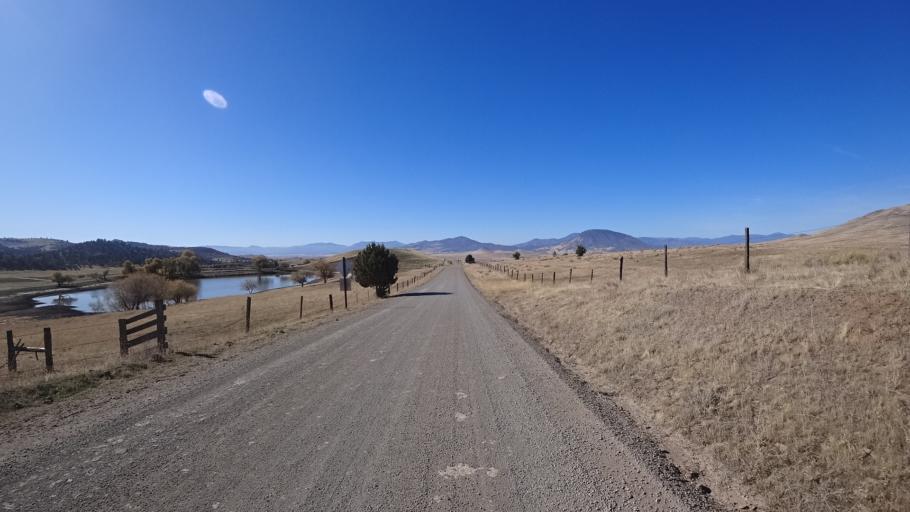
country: US
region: California
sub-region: Siskiyou County
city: Montague
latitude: 41.8154
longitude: -122.3644
